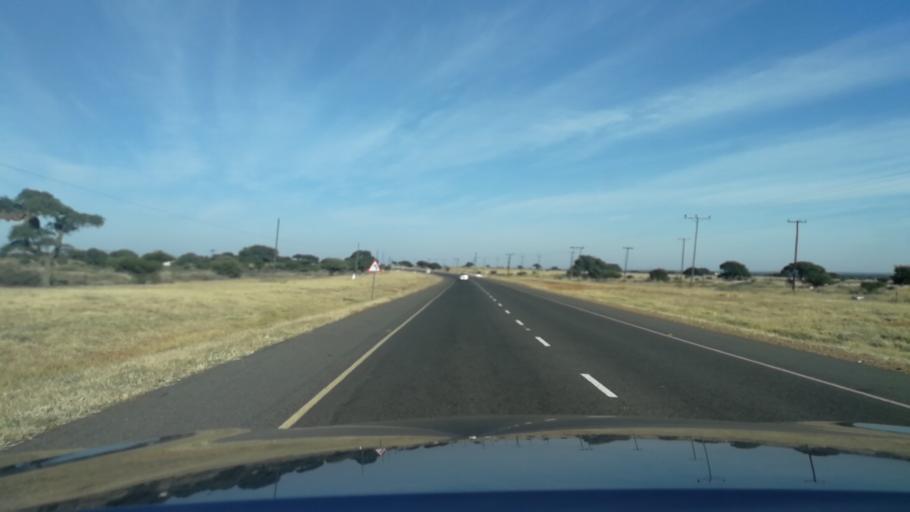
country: BW
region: South East
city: Janeng
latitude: -25.4740
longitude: 25.5232
